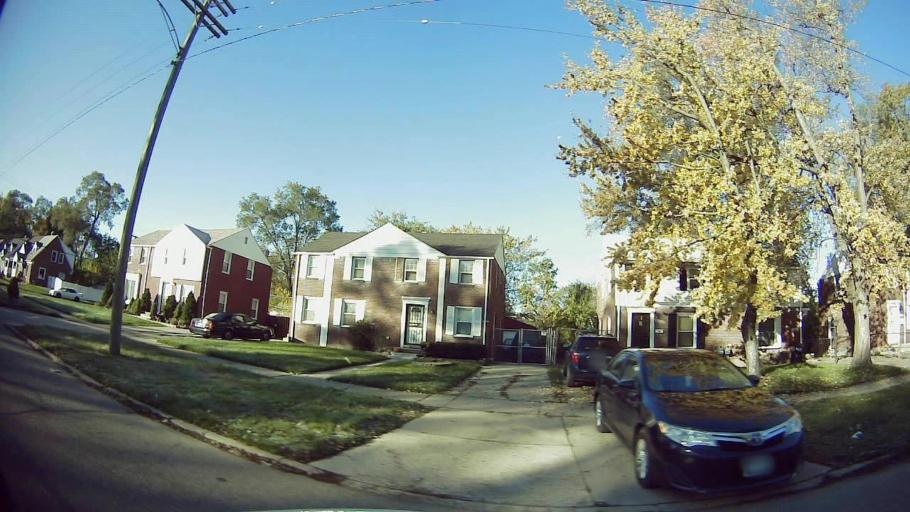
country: US
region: Michigan
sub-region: Oakland County
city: Oak Park
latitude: 42.4411
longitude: -83.1710
